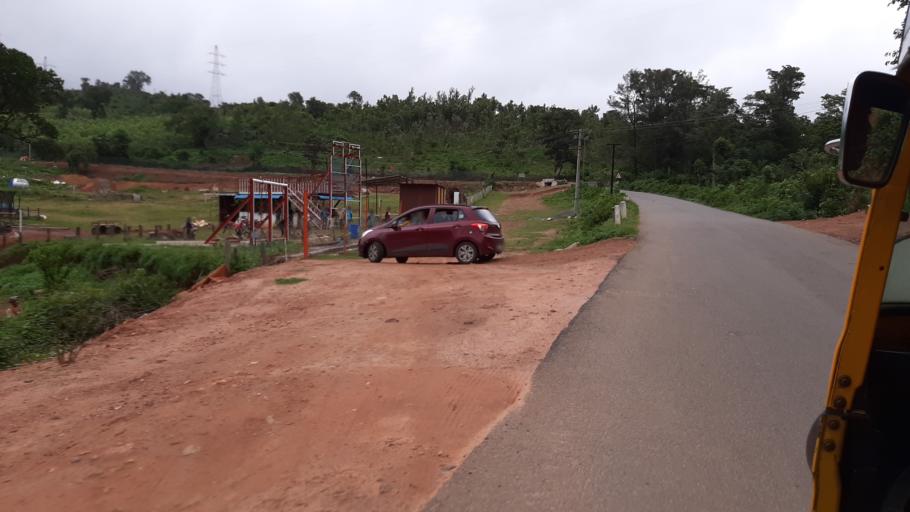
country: IN
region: Andhra Pradesh
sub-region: Vizianagaram District
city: Salur
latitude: 18.2409
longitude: 82.9991
